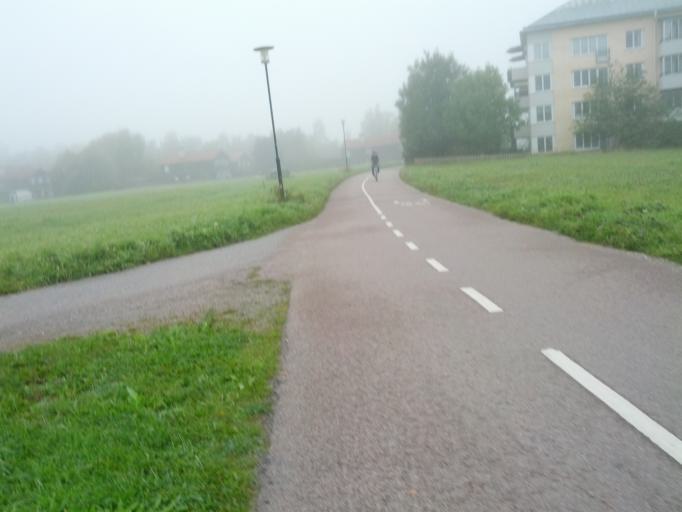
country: SE
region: Uppsala
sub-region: Uppsala Kommun
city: Uppsala
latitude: 59.8432
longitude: 17.6347
